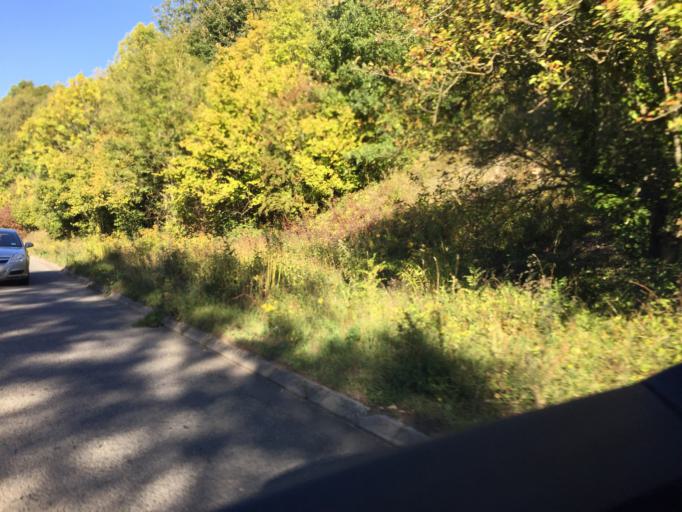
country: GB
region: England
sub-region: Wiltshire
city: Biddestone
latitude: 51.4711
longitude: -2.2127
